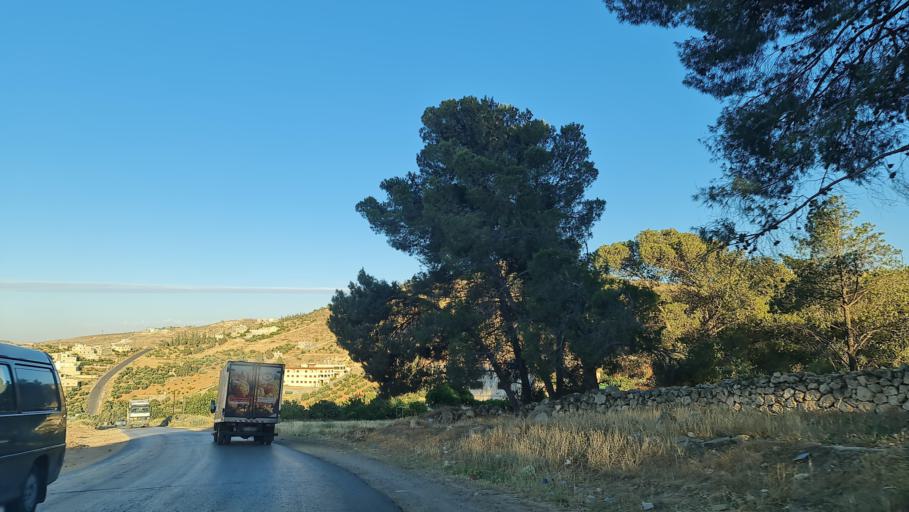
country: JO
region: Amman
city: Al Jubayhah
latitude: 32.0914
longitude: 35.9317
